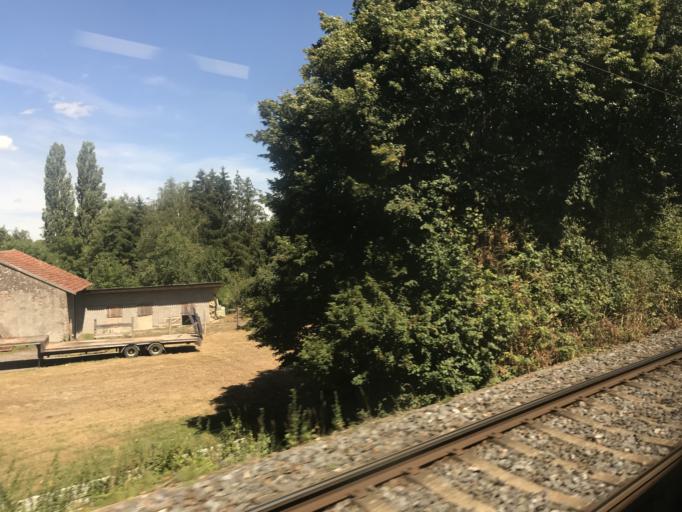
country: FR
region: Lorraine
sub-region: Departement de la Moselle
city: Sarrebourg
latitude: 48.8119
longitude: 7.0039
